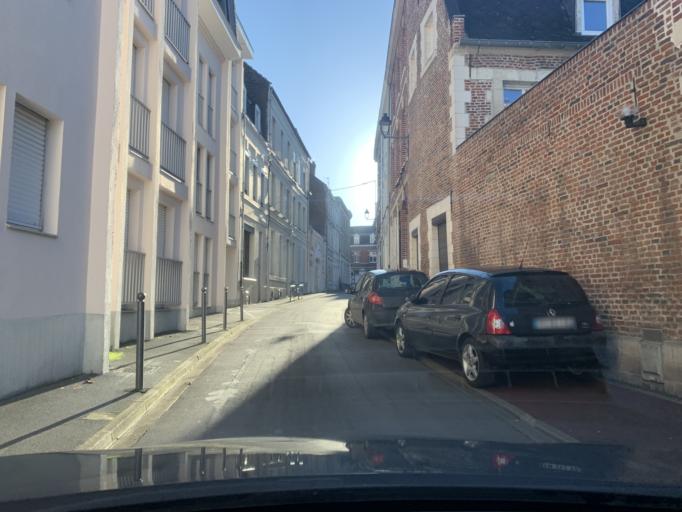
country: FR
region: Nord-Pas-de-Calais
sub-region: Departement du Nord
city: Cambrai
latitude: 50.1780
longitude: 3.2336
